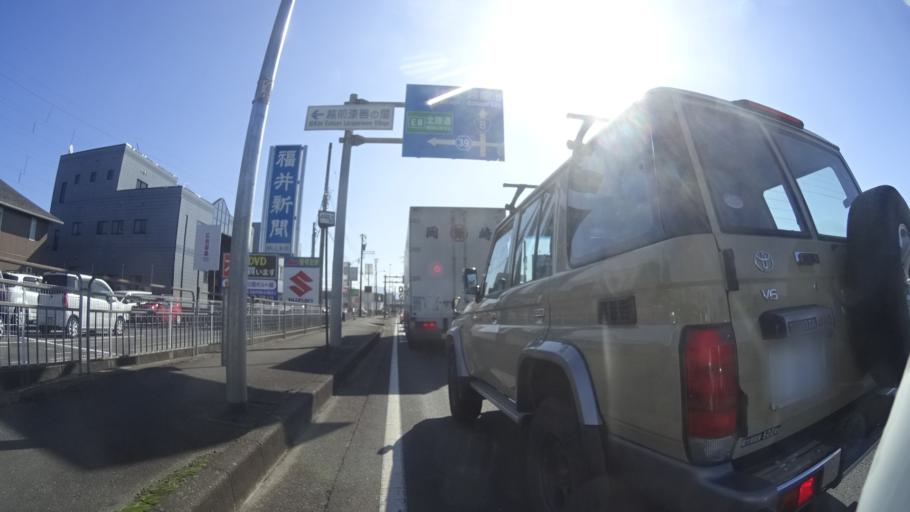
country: JP
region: Fukui
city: Sabae
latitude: 35.9505
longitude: 136.1926
